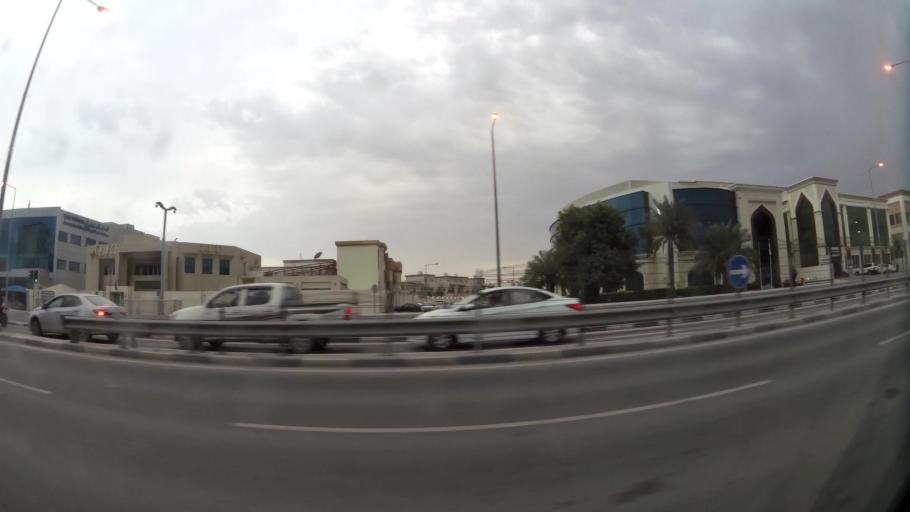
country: QA
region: Baladiyat ad Dawhah
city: Doha
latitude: 25.2652
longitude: 51.5182
